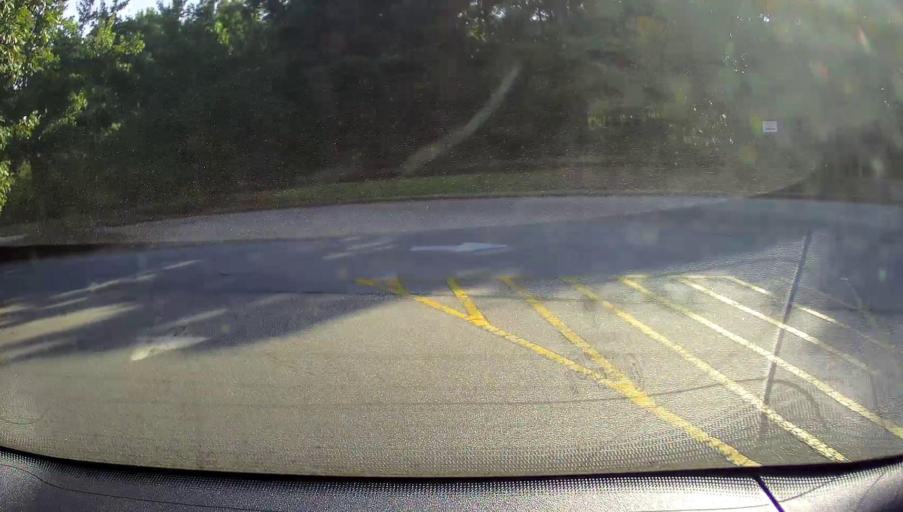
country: US
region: Georgia
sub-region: Fayette County
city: Peachtree City
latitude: 33.3994
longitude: -84.6006
